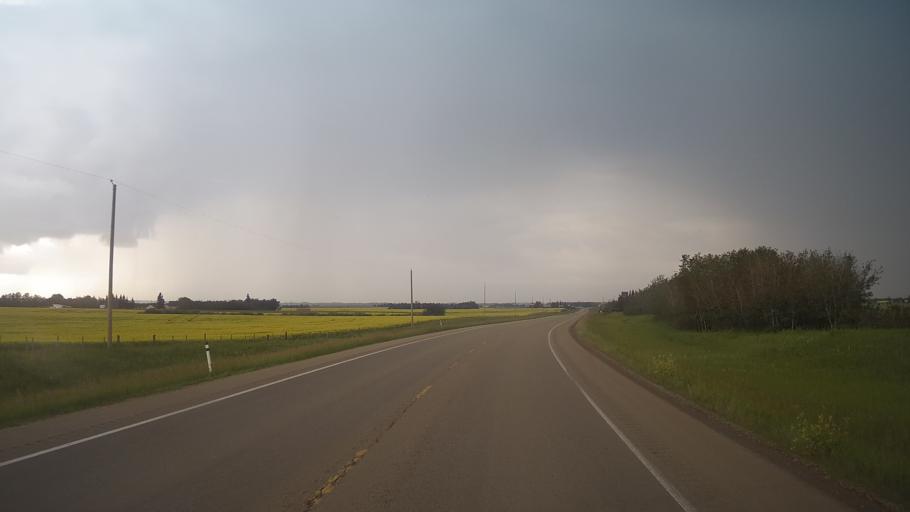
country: CA
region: Alberta
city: Tofield
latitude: 53.3230
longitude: -112.5519
